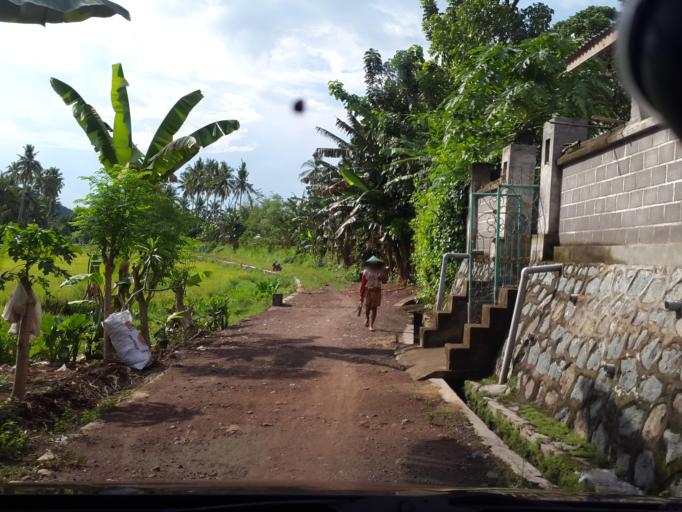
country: ID
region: West Nusa Tenggara
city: Ranggagata
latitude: -8.7020
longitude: 116.1360
